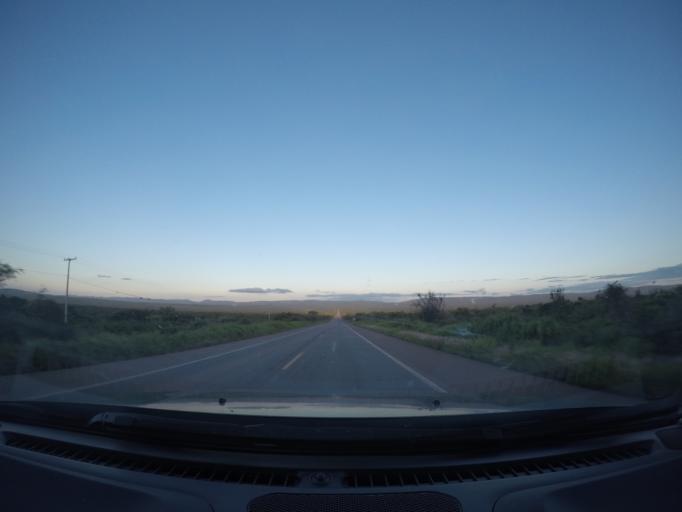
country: BR
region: Bahia
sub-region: Seabra
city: Seabra
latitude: -12.4104
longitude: -41.9697
